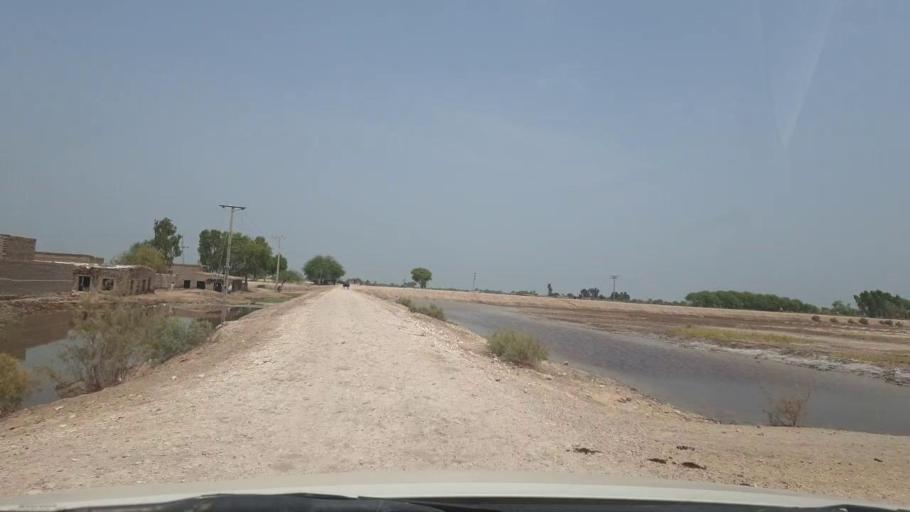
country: PK
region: Sindh
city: Rustam jo Goth
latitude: 28.0777
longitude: 68.8182
